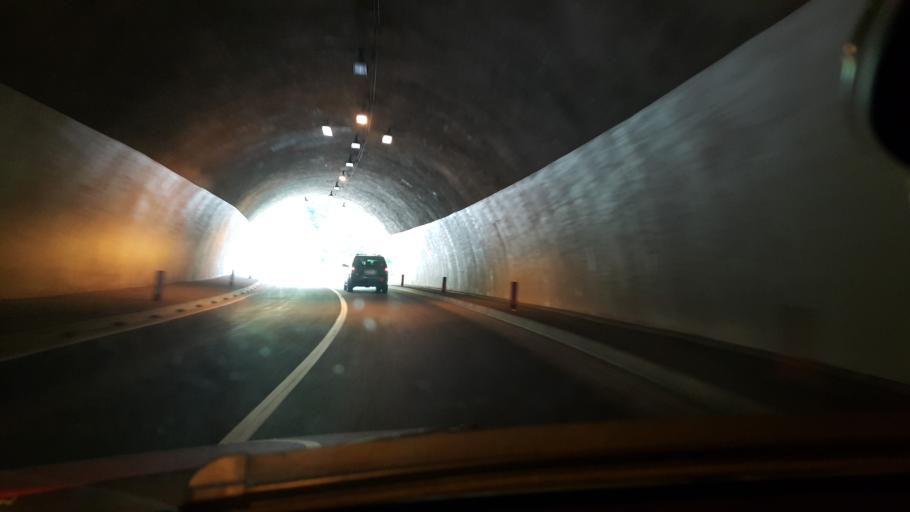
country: SI
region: Trzic
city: Trzic
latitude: 46.3609
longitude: 14.3008
